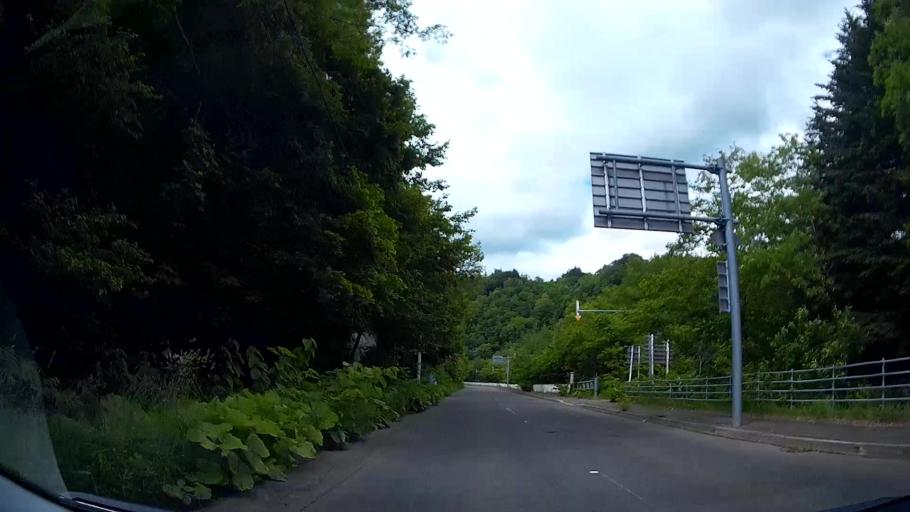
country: JP
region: Hokkaido
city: Kitahiroshima
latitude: 42.8587
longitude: 141.4135
